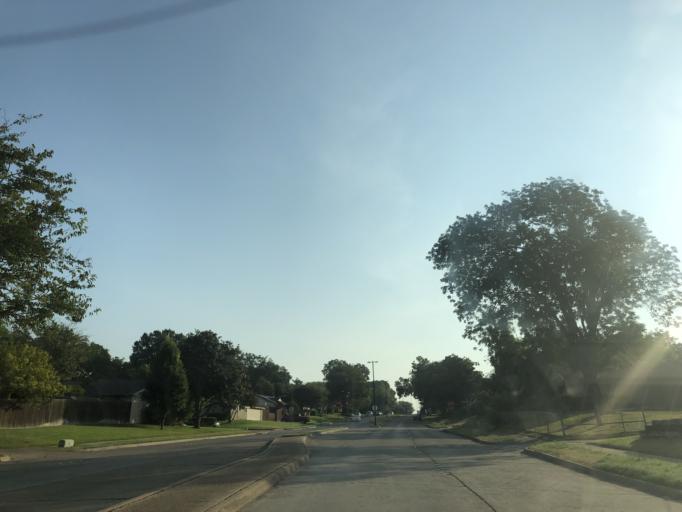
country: US
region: Texas
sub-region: Dallas County
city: Garland
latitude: 32.8674
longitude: -96.6242
